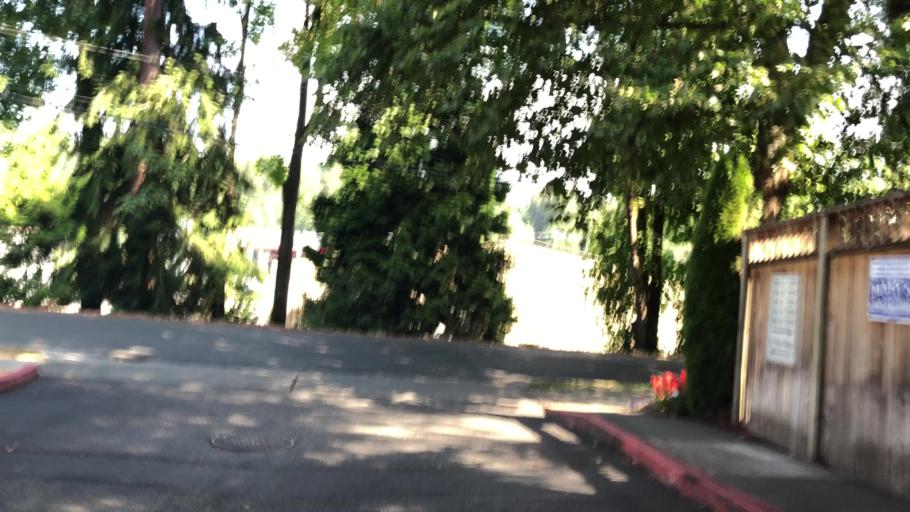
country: US
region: Washington
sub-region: King County
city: Kingsgate
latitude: 47.7105
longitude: -122.1654
